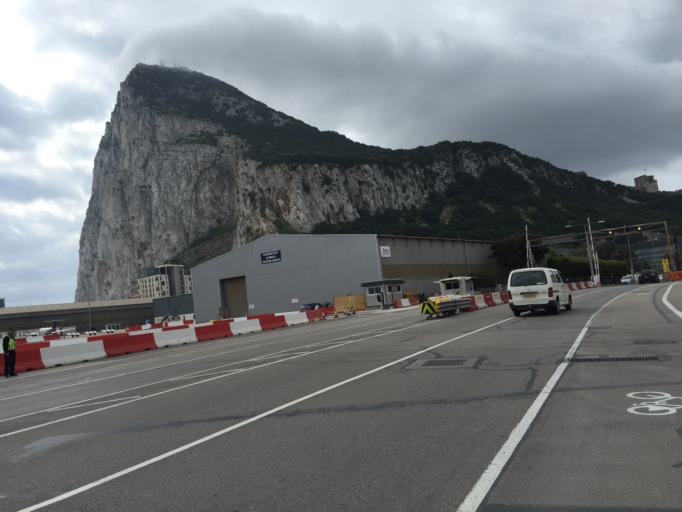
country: GI
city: Gibraltar
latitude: 36.1507
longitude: -5.3489
